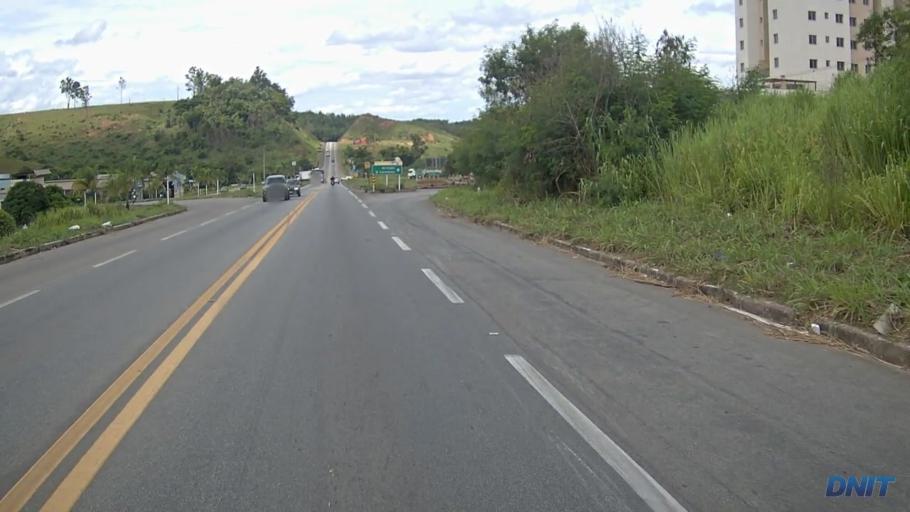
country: BR
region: Minas Gerais
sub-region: Ipatinga
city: Ipatinga
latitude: -19.4556
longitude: -42.5232
